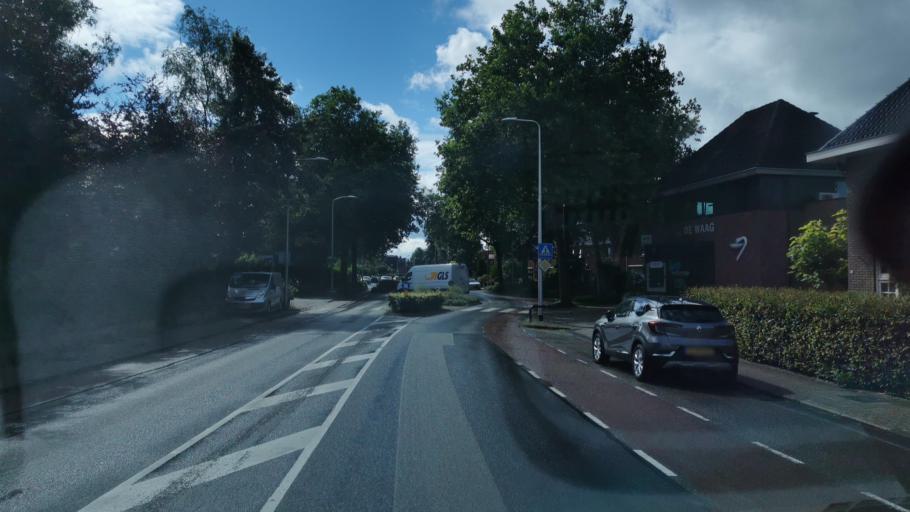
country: NL
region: Overijssel
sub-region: Gemeente Haaksbergen
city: Haaksbergen
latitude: 52.1610
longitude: 6.7329
